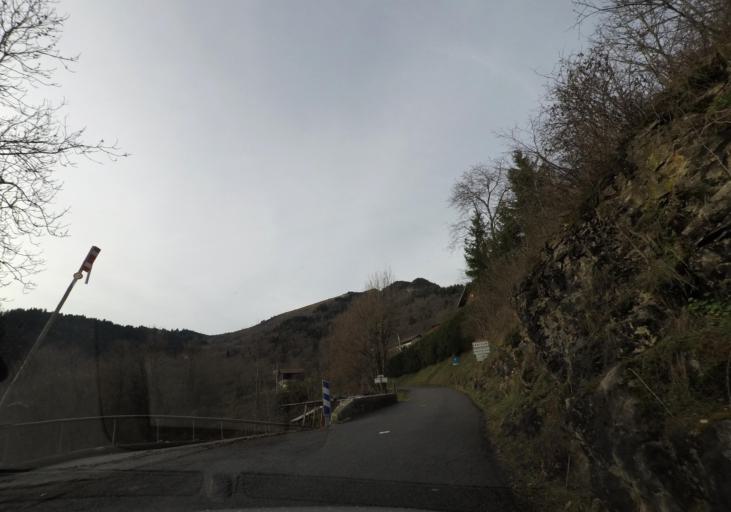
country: FR
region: Rhone-Alpes
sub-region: Departement de la Haute-Savoie
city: Ayse
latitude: 46.0522
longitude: 6.4496
